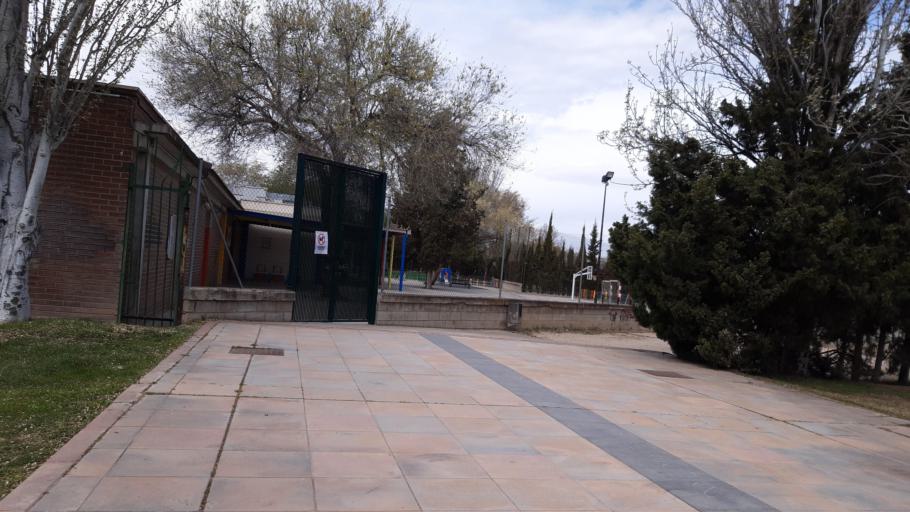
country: ES
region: Aragon
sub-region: Provincia de Zaragoza
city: Utebo
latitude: 41.7104
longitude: -0.9987
